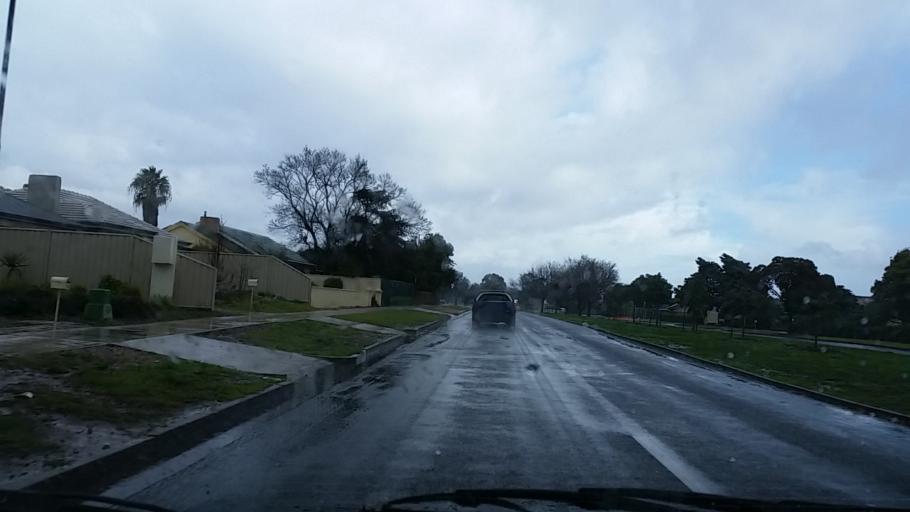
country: AU
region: South Australia
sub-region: Salisbury
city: Elizabeth
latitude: -34.7109
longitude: 138.6835
